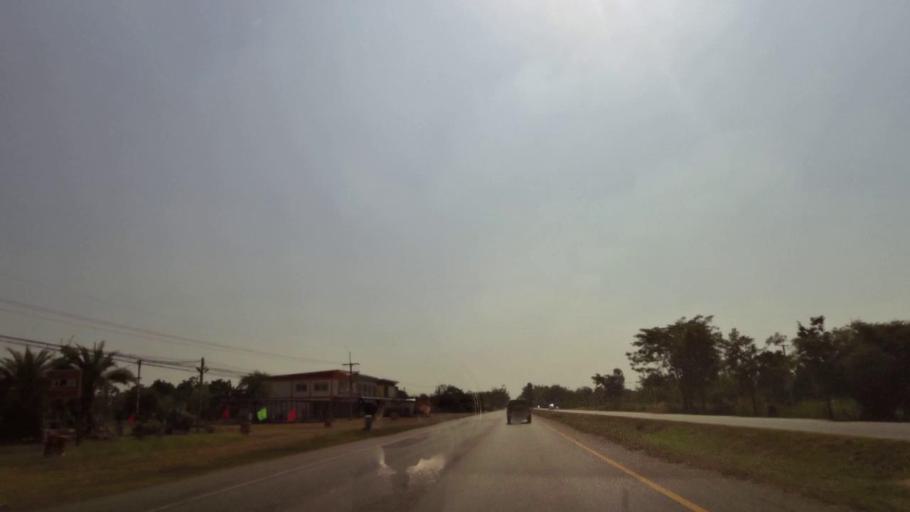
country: TH
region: Phichit
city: Bueng Na Rang
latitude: 16.3342
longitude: 100.1284
